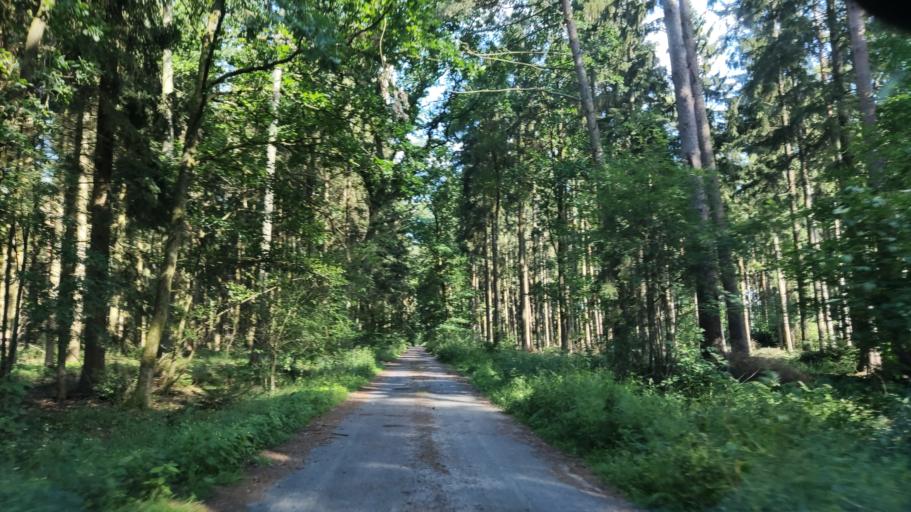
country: DE
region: Lower Saxony
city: Hanstedt Eins
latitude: 53.0821
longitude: 10.4107
